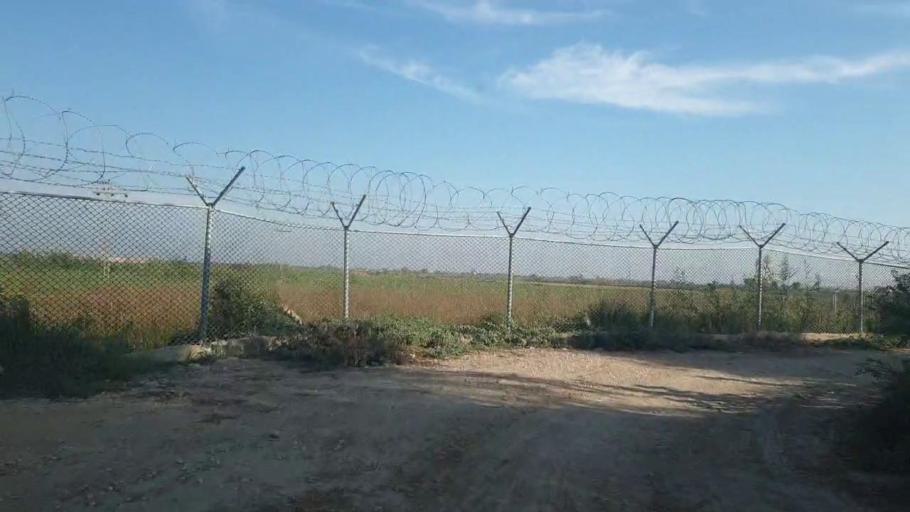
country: PK
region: Sindh
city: Talhar
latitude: 24.8413
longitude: 68.8530
